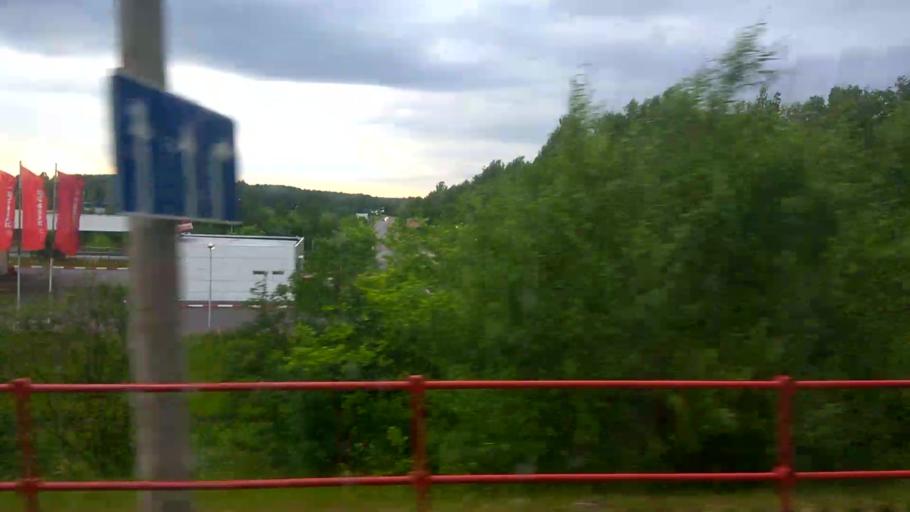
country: RU
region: Moskovskaya
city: Kashira
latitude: 54.8502
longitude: 38.2192
